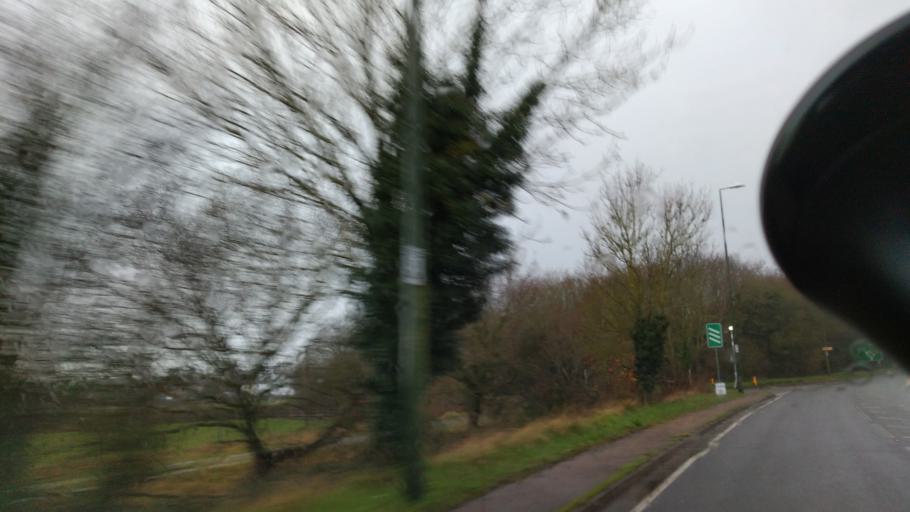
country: GB
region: England
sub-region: West Sussex
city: Arundel
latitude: 50.8504
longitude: -0.5572
